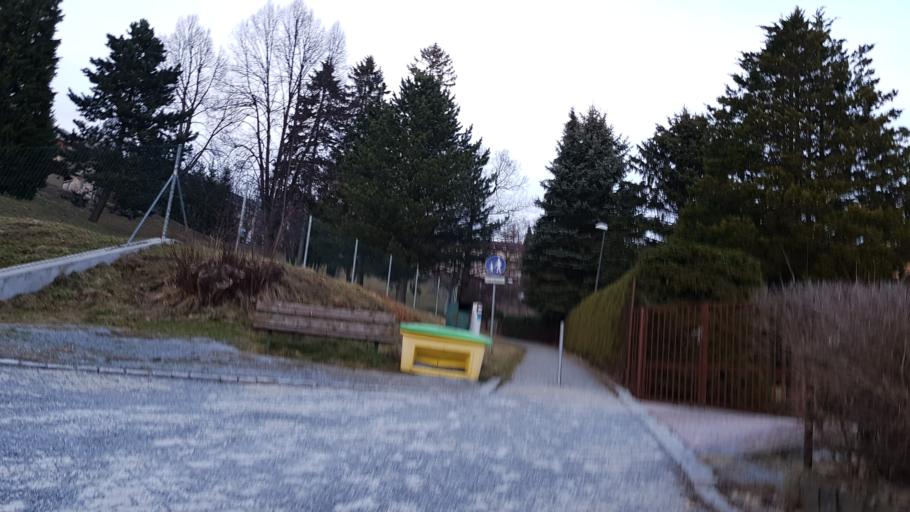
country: CZ
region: Olomoucky
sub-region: Okres Jesenik
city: Jesenik
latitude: 50.2378
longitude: 17.1862
